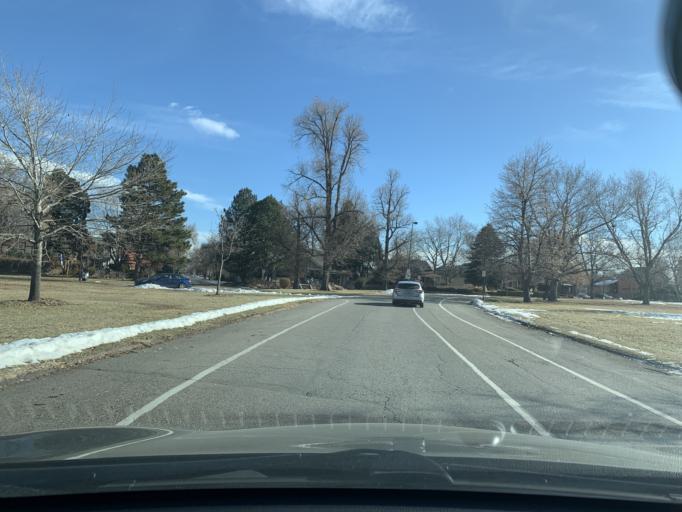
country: US
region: Colorado
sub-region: Jefferson County
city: Edgewater
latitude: 39.7522
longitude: -105.0439
